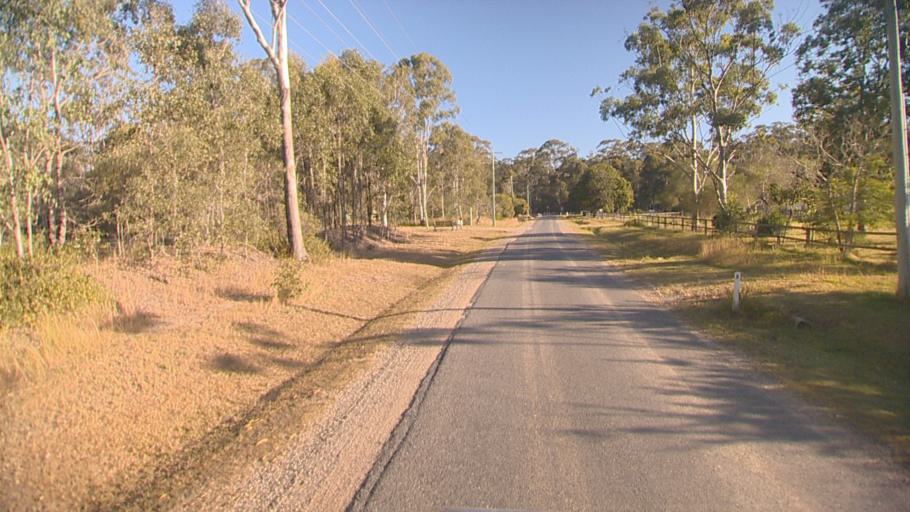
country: AU
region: Queensland
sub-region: Logan
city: Chambers Flat
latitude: -27.7776
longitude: 153.1281
